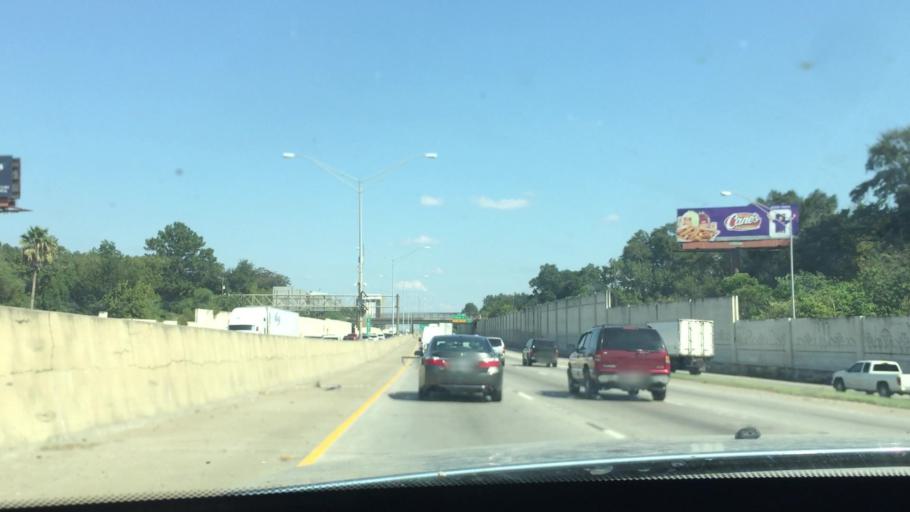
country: US
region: Louisiana
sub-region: East Baton Rouge Parish
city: Baton Rouge
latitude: 30.4240
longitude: -91.1494
